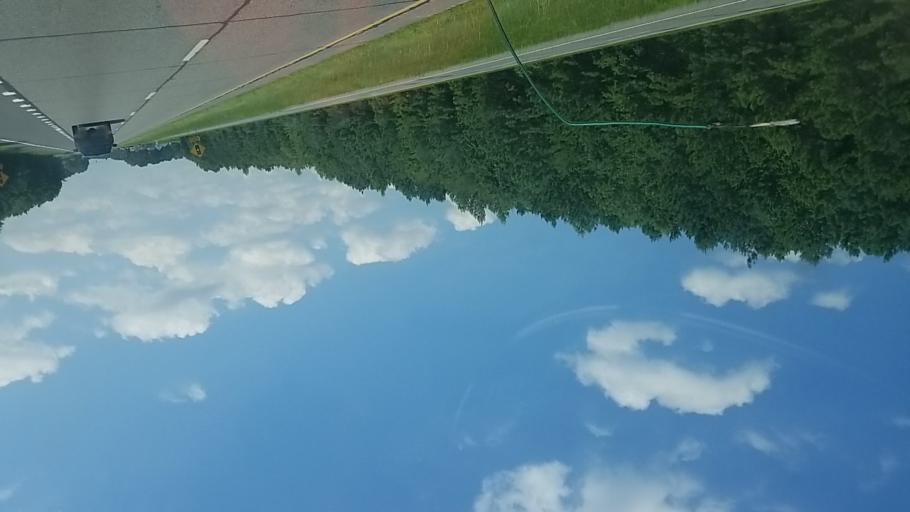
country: US
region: Delaware
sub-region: Sussex County
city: Georgetown
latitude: 38.7423
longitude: -75.4263
